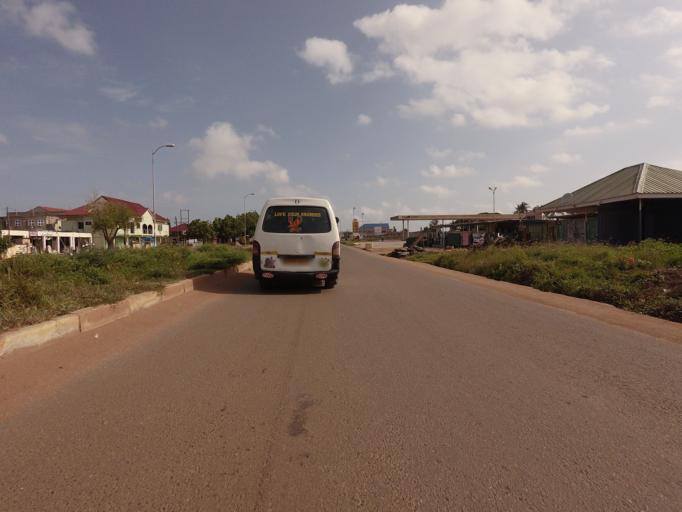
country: GH
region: Greater Accra
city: Tema
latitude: 5.6701
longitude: -0.0468
